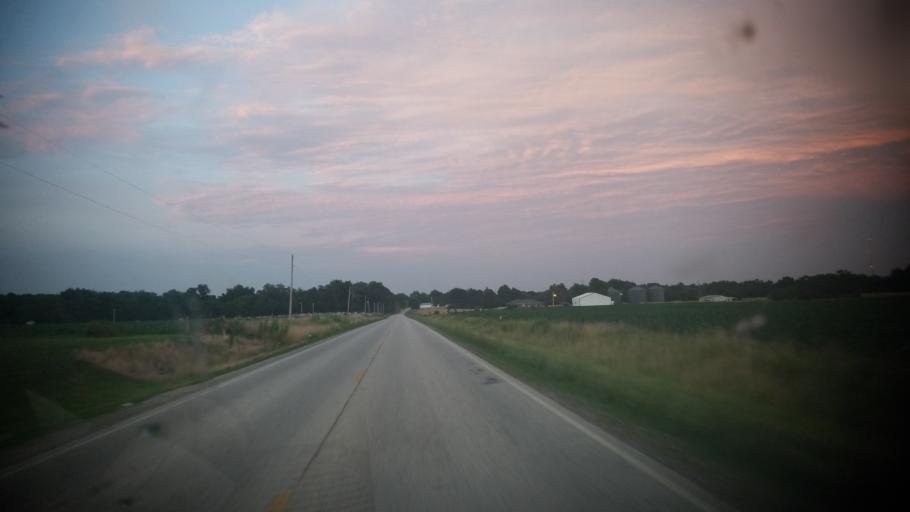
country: US
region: Illinois
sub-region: Clay County
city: Flora
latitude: 38.5160
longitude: -88.4527
